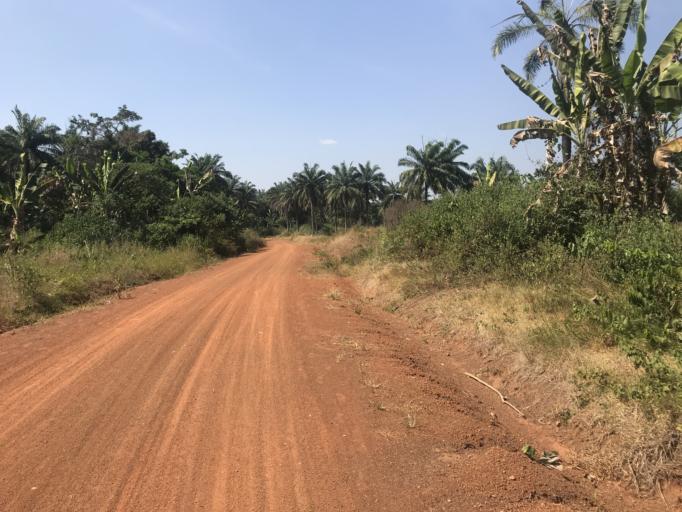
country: NG
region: Osun
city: Ikirun
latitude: 7.9341
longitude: 4.6229
